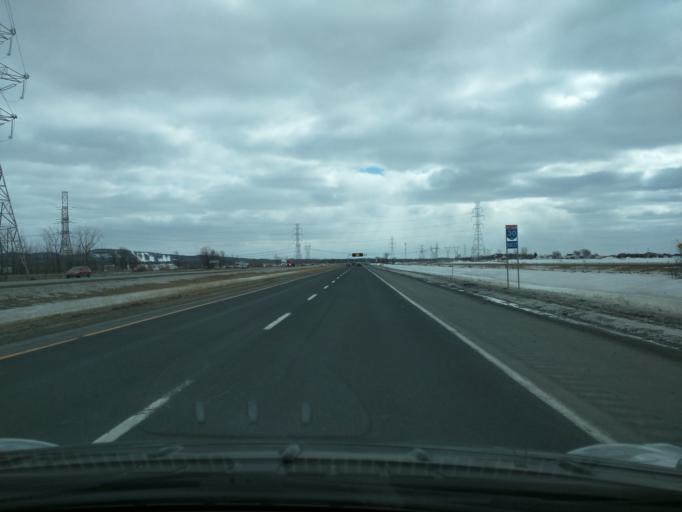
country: CA
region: Quebec
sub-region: Monteregie
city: Sainte-Julie
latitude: 45.6006
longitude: -73.3741
